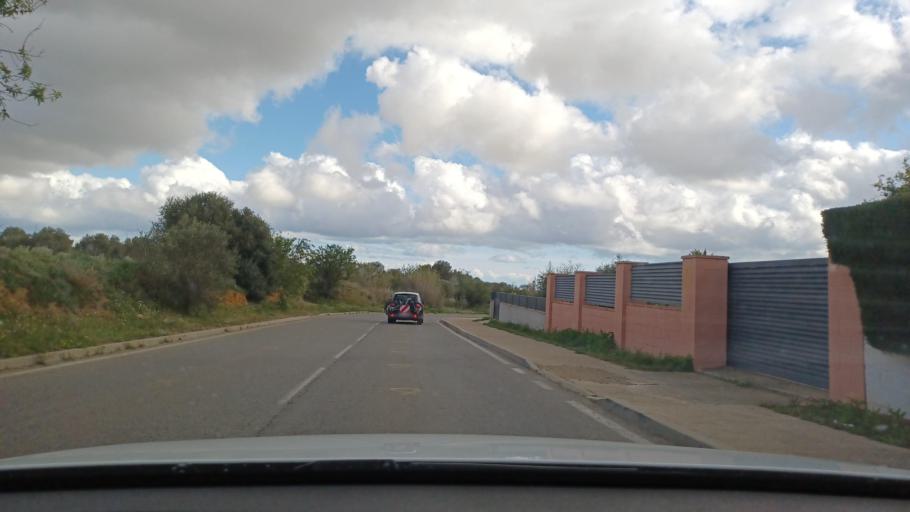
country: ES
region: Catalonia
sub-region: Provincia de Tarragona
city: Botarell
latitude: 41.1335
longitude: 0.9936
